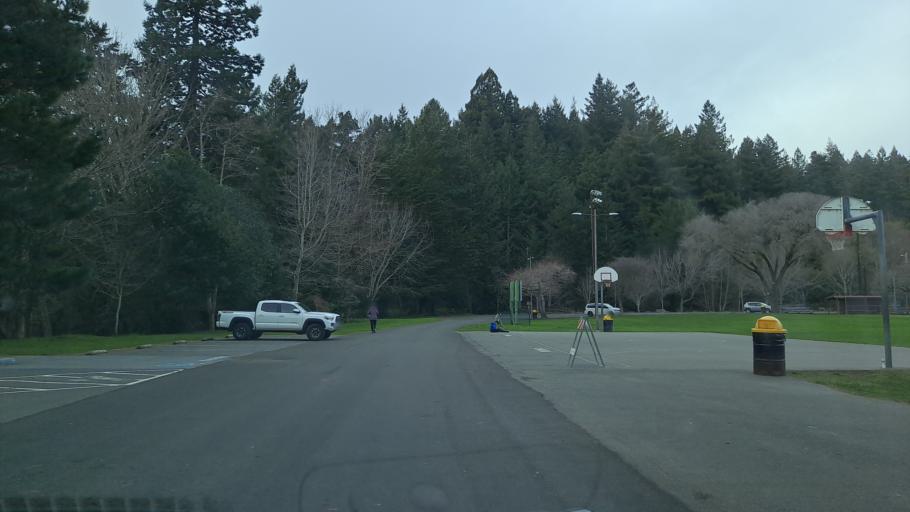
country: US
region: California
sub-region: Humboldt County
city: Fortuna
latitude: 40.6007
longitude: -124.1510
